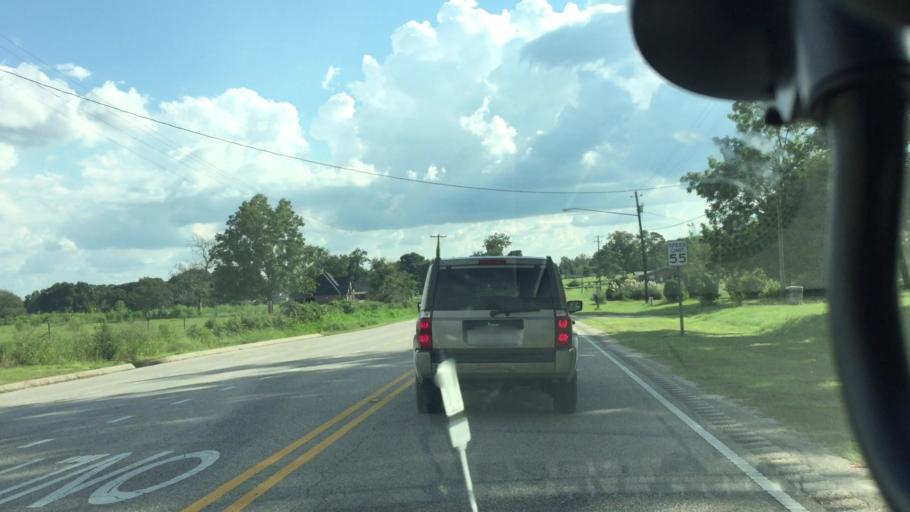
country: US
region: Alabama
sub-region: Coffee County
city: Enterprise
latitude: 31.3703
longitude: -85.8258
